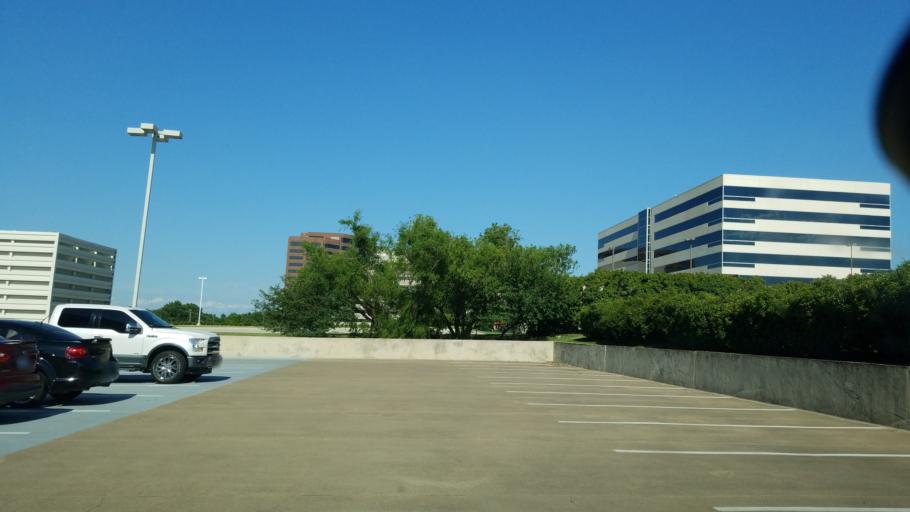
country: US
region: Texas
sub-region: Dallas County
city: Irving
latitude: 32.8887
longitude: -96.9698
